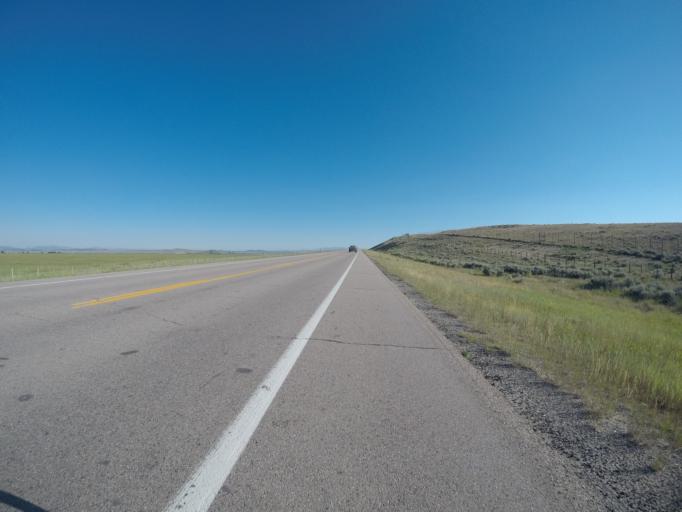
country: US
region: Wyoming
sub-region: Sublette County
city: Pinedale
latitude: 42.9413
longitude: -110.0830
